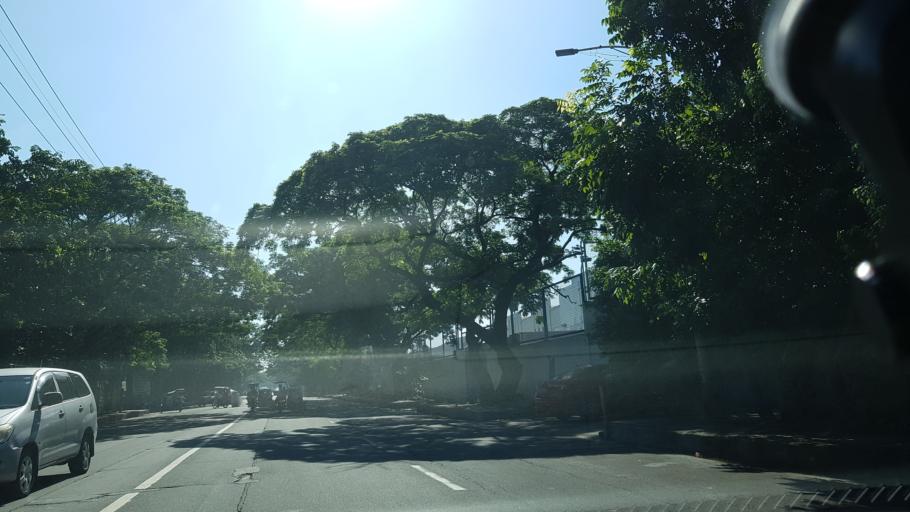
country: PH
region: Calabarzon
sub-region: Province of Rizal
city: Cainta
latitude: 14.5674
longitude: 121.0908
